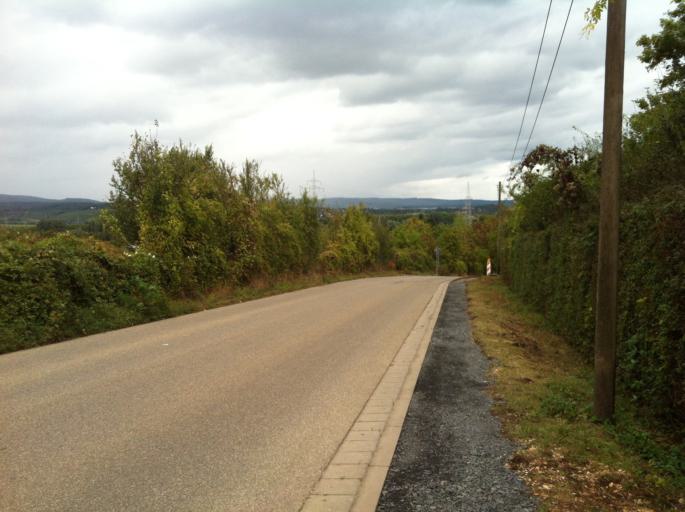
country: DE
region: Rheinland-Pfalz
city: Budenheim
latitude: 50.0273
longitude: 8.1851
